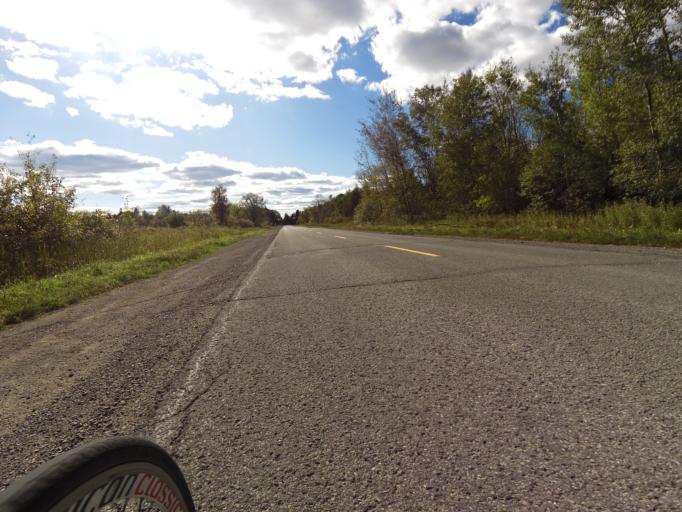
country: CA
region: Ontario
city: Bells Corners
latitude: 45.1012
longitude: -75.6355
